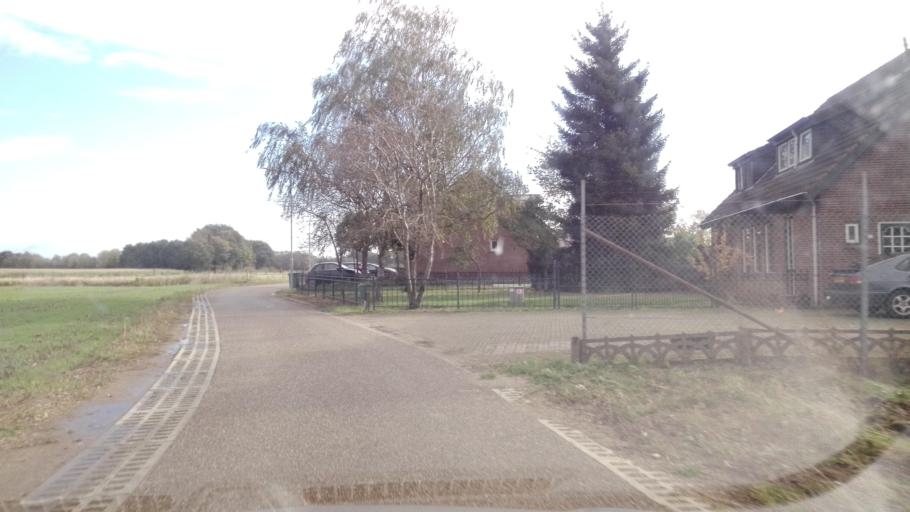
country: NL
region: Limburg
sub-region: Gemeente Venlo
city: Venlo
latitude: 51.4170
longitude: 6.1734
